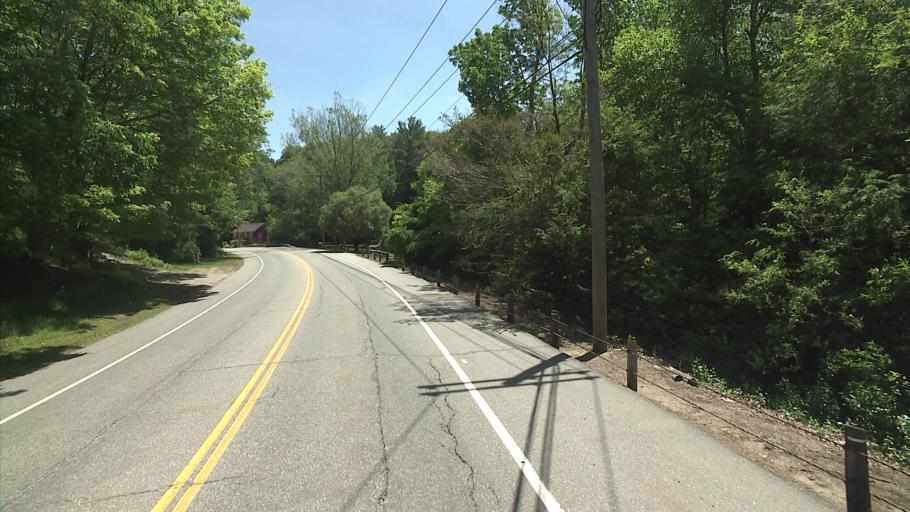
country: US
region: Connecticut
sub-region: Tolland County
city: Stafford
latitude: 41.9929
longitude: -72.2650
